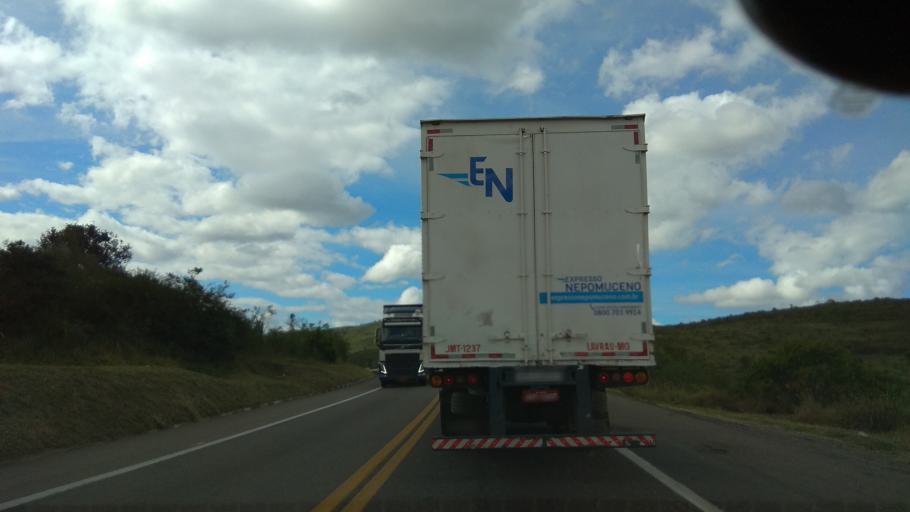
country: BR
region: Bahia
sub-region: Amargosa
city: Amargosa
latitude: -12.9125
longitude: -39.8662
